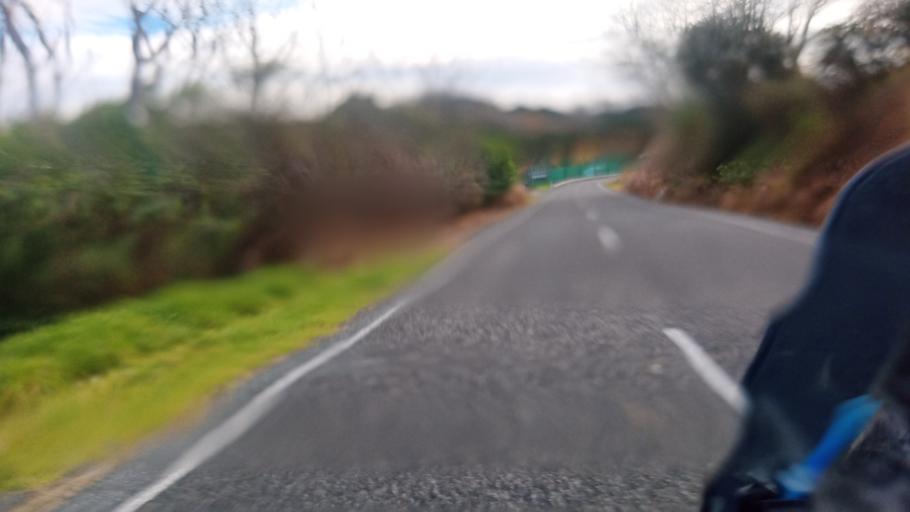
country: NZ
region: Gisborne
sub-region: Gisborne District
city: Gisborne
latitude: -38.4555
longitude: 177.8729
